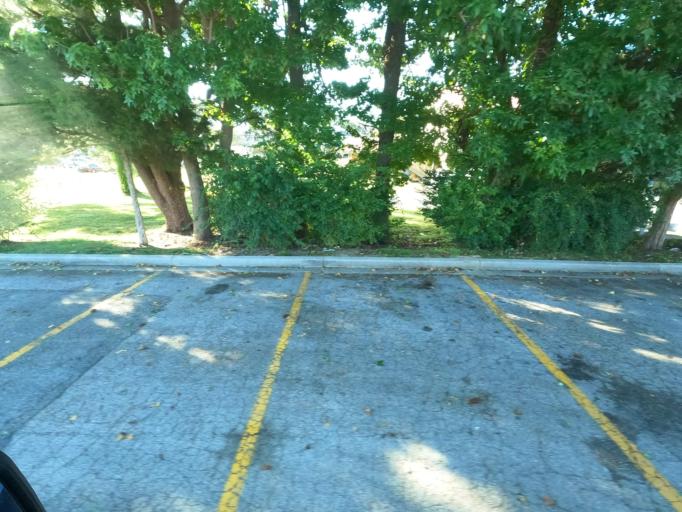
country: US
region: Tennessee
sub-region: Coffee County
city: Manchester
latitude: 35.4547
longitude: -86.0473
